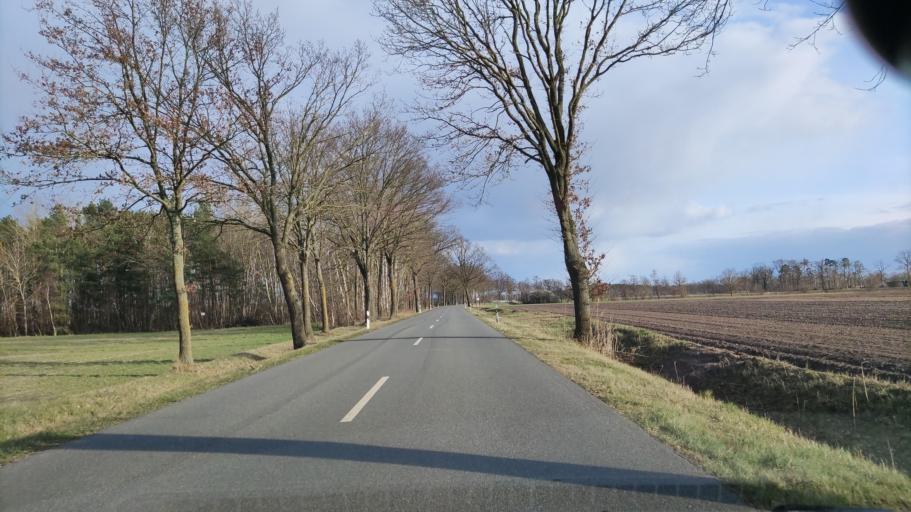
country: DE
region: Lower Saxony
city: Klein Gusborn
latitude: 53.0665
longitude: 11.2288
